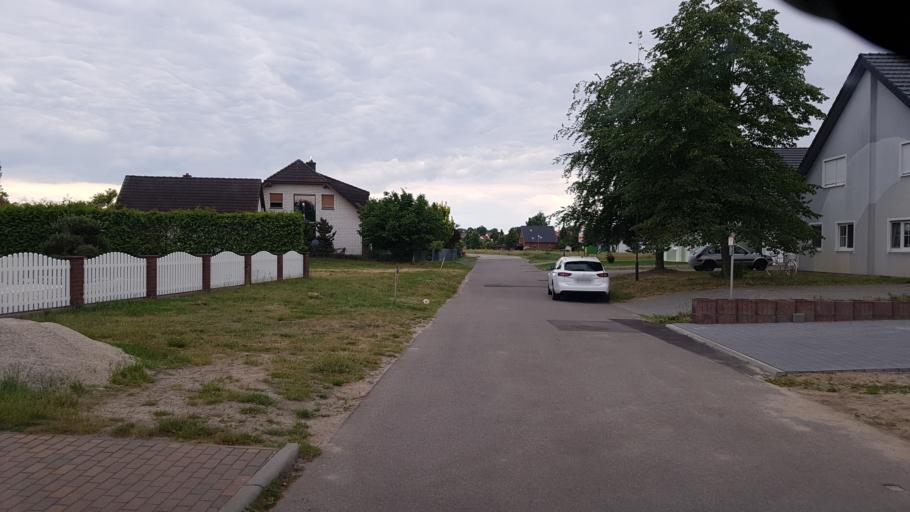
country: DE
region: Saxony-Anhalt
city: Holzdorf
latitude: 51.8186
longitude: 13.2265
